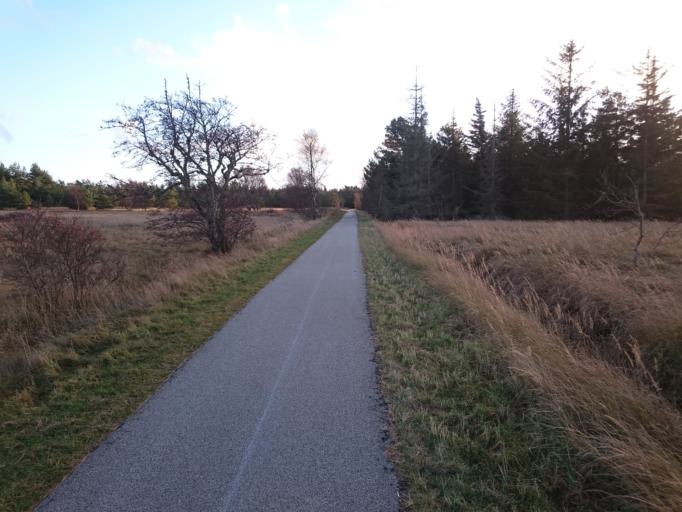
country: DK
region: North Denmark
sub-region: Frederikshavn Kommune
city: Skagen
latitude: 57.7076
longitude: 10.5238
